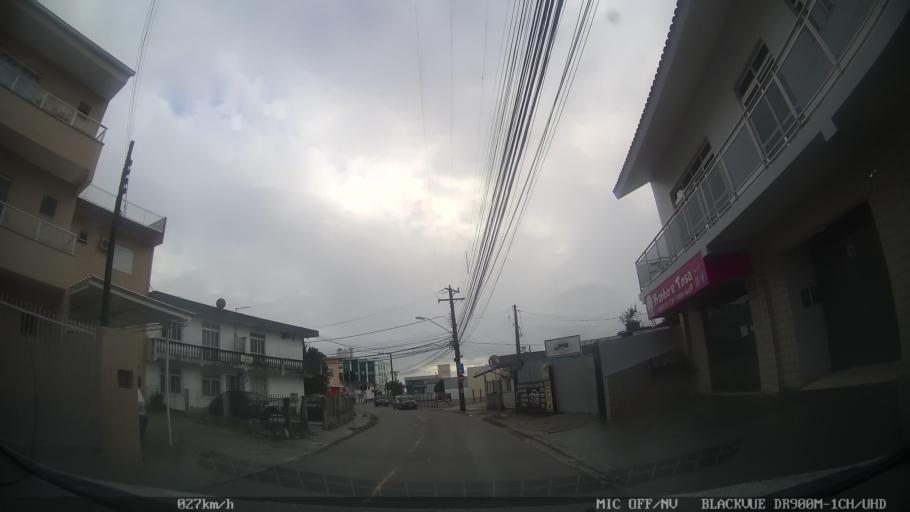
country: BR
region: Santa Catarina
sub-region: Sao Jose
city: Campinas
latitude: -27.5722
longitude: -48.6061
